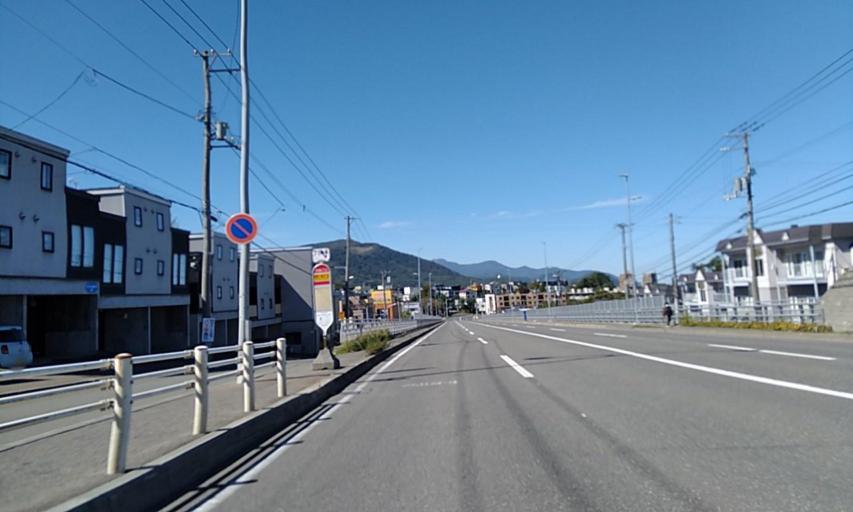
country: JP
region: Hokkaido
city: Sapporo
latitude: 43.0087
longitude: 141.3782
